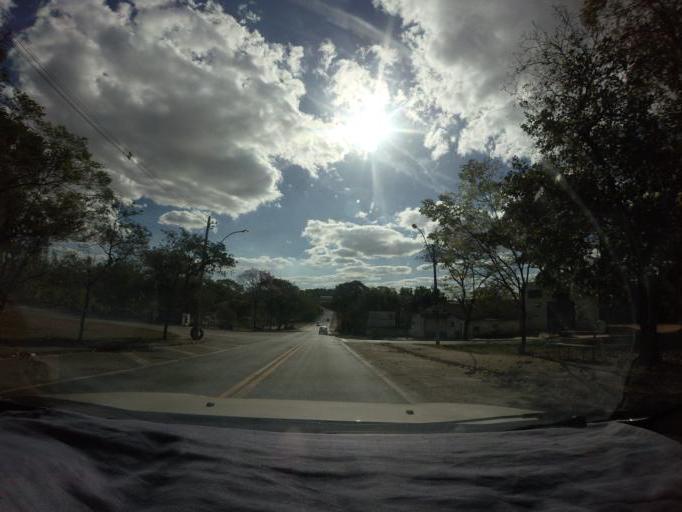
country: BR
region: Sao Paulo
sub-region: Santa Barbara D'Oeste
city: Santa Barbara d'Oeste
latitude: -22.7441
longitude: -47.5286
